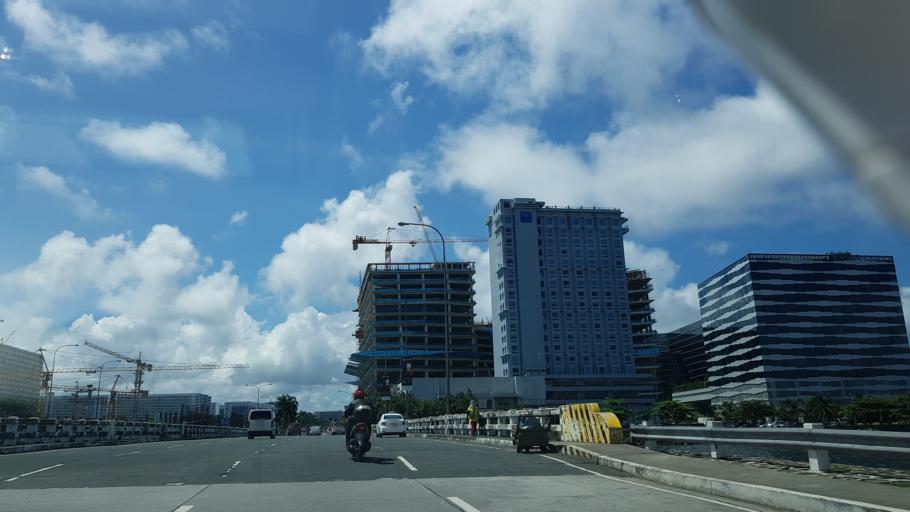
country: PH
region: Metro Manila
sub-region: City of Manila
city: Port Area
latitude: 14.5439
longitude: 120.9825
